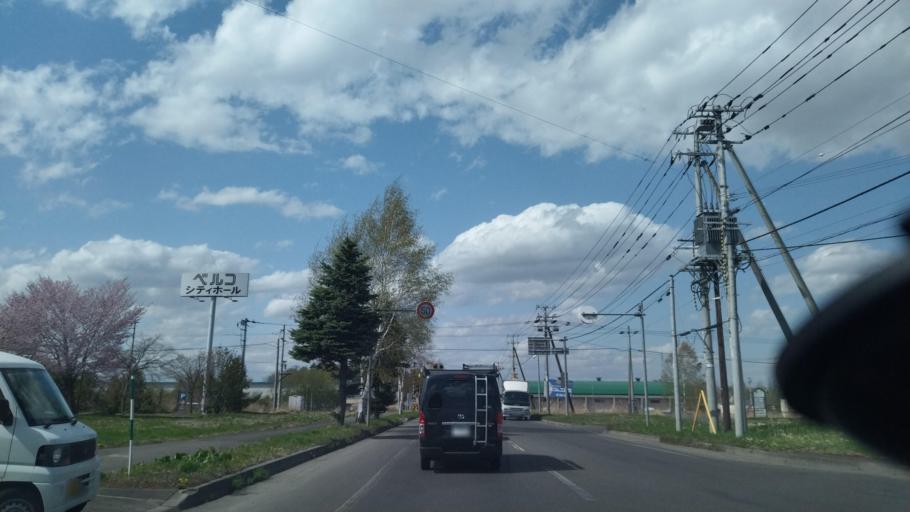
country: JP
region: Hokkaido
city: Obihiro
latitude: 42.9243
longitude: 143.1436
